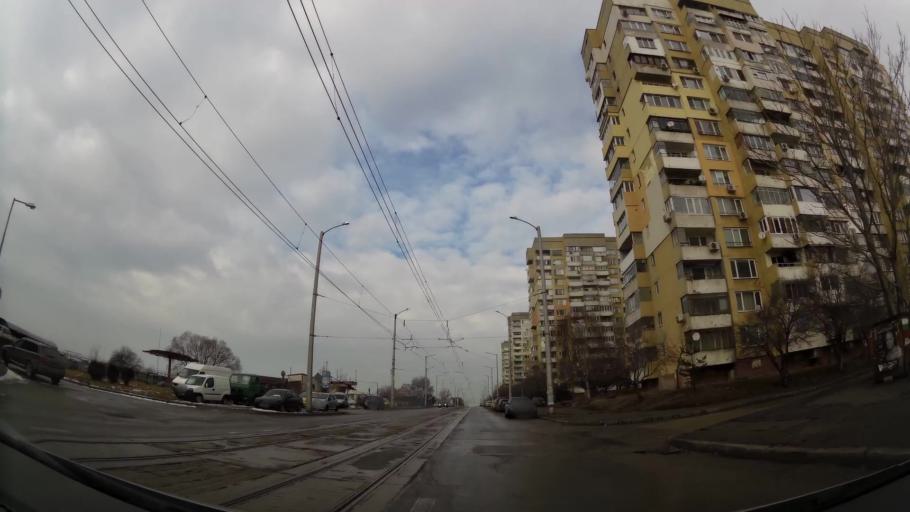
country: BG
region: Sofiya
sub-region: Obshtina Bozhurishte
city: Bozhurishte
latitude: 42.7106
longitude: 23.2436
